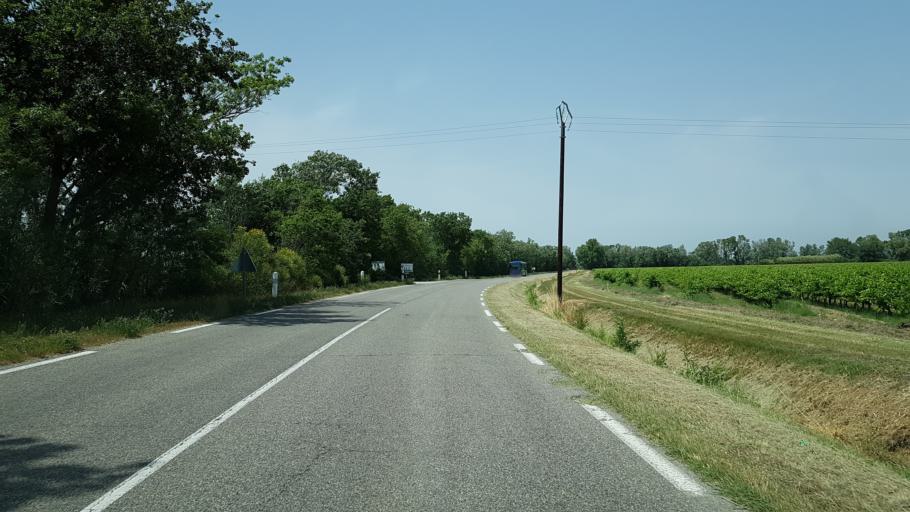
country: FR
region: Provence-Alpes-Cote d'Azur
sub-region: Departement des Bouches-du-Rhone
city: Saint-Martin-de-Crau
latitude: 43.5203
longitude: 4.7423
